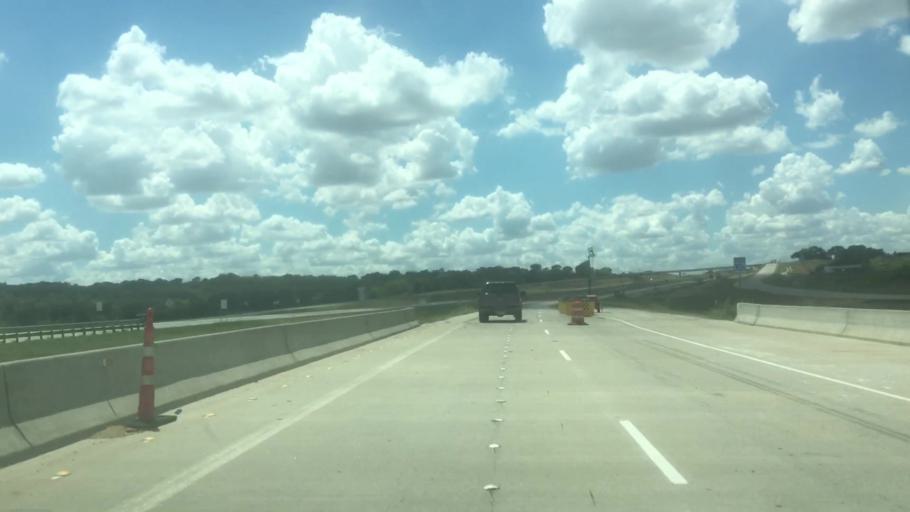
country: US
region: Texas
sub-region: Caldwell County
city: Lockhart
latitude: 29.8590
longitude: -97.7108
